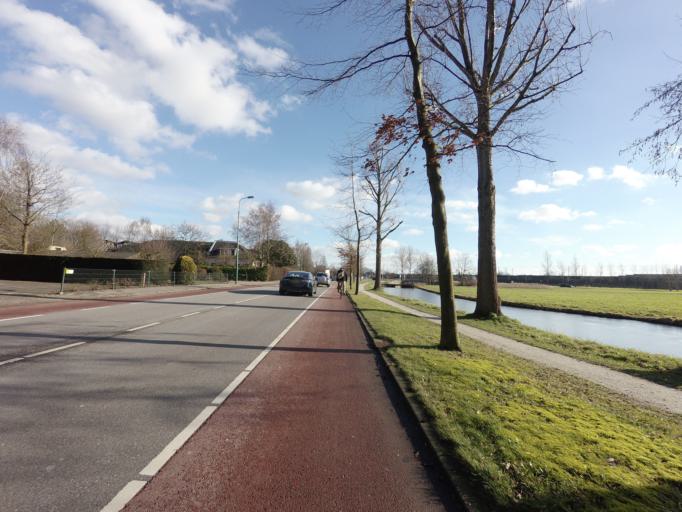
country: NL
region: Utrecht
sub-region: Stichtse Vecht
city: Spechtenkamp
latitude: 52.1045
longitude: 5.0196
